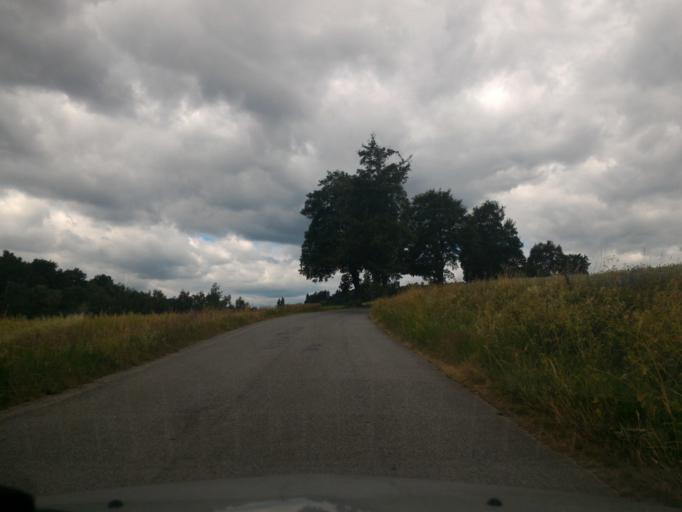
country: CZ
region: Vysocina
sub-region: Okres Jihlava
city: Telc
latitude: 49.2048
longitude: 15.4215
